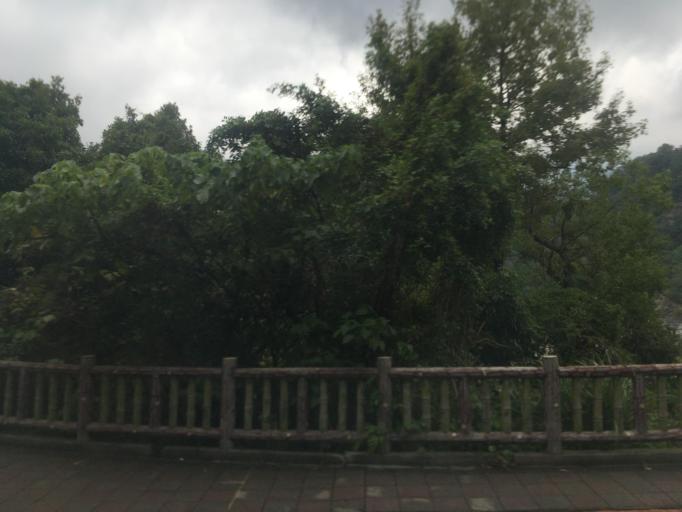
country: TW
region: Taipei
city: Taipei
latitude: 25.1426
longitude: 121.5277
